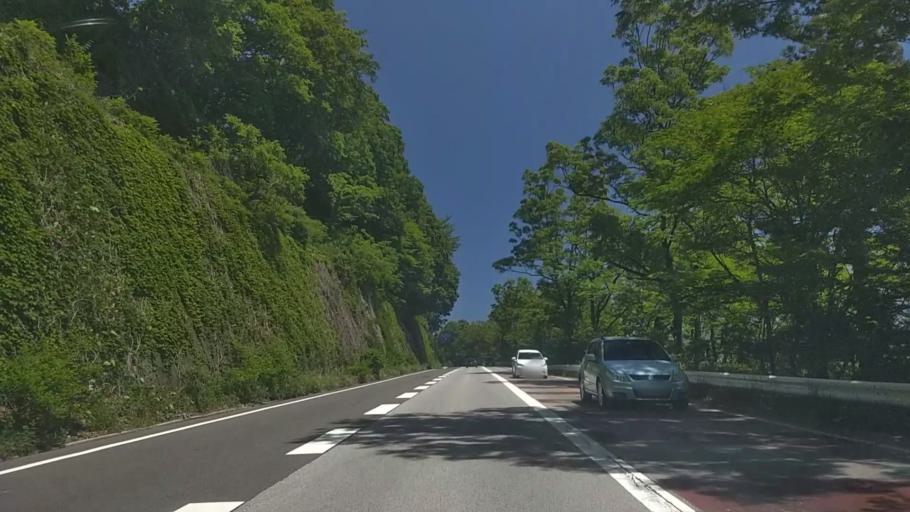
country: JP
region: Yamanashi
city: Nirasaki
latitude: 35.8040
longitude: 138.4269
